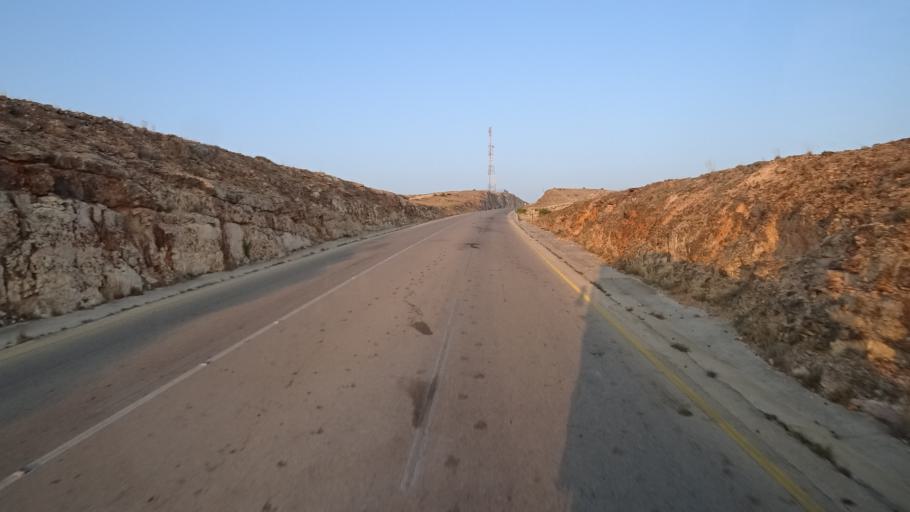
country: OM
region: Zufar
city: Salalah
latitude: 16.8231
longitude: 53.6442
